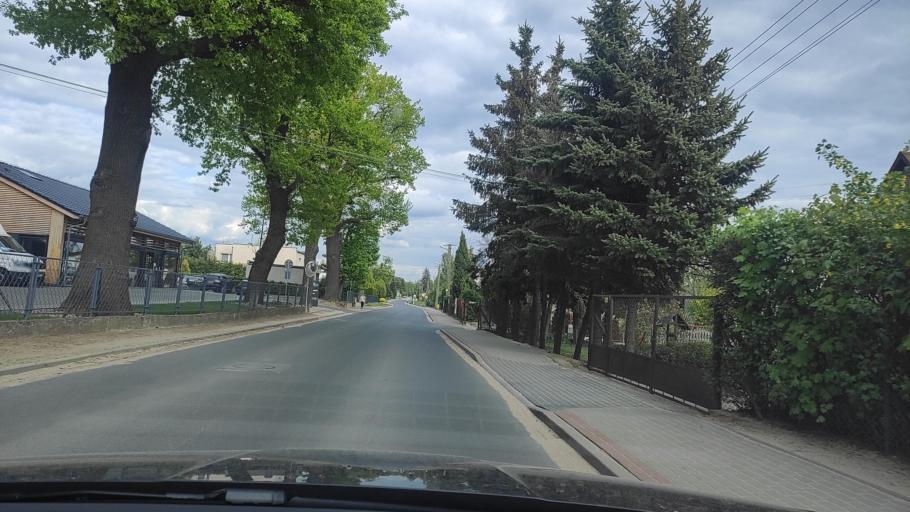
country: PL
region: Greater Poland Voivodeship
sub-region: Powiat poznanski
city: Kostrzyn
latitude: 52.4607
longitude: 17.1750
